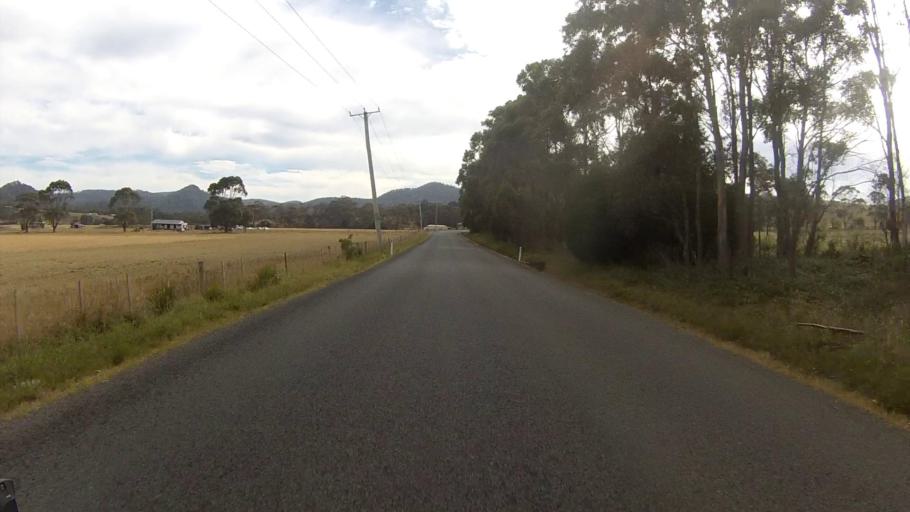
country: AU
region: Tasmania
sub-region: Sorell
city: Sorell
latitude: -42.7918
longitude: 147.7990
